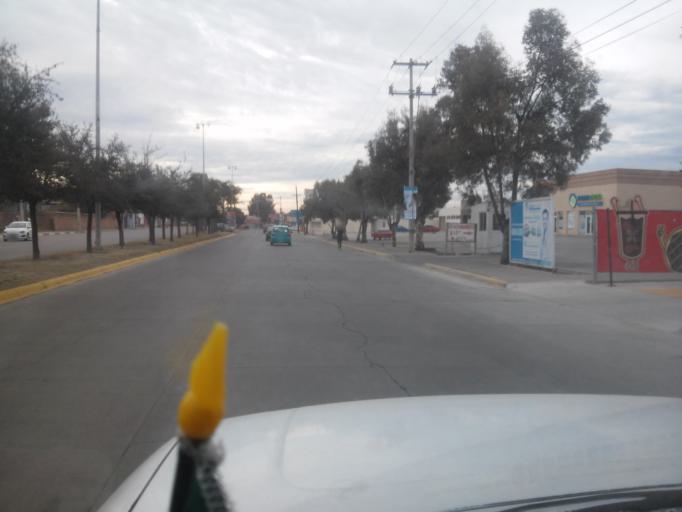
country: MX
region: Durango
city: Victoria de Durango
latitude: 24.0011
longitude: -104.6488
